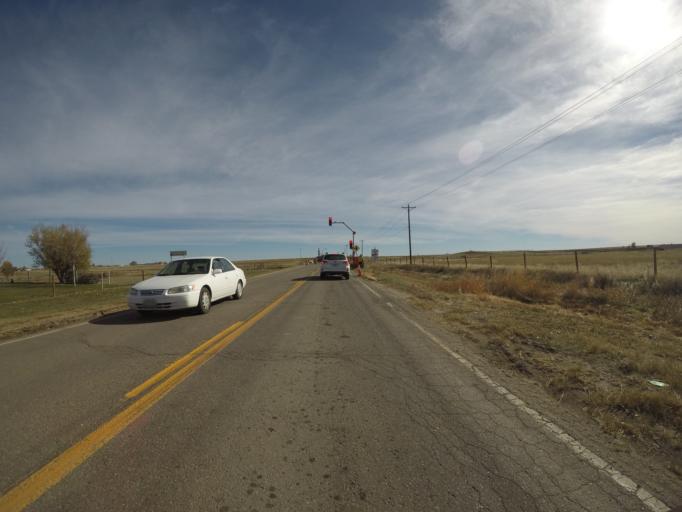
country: US
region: Colorado
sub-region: Adams County
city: Strasburg
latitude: 39.7384
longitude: -104.3173
